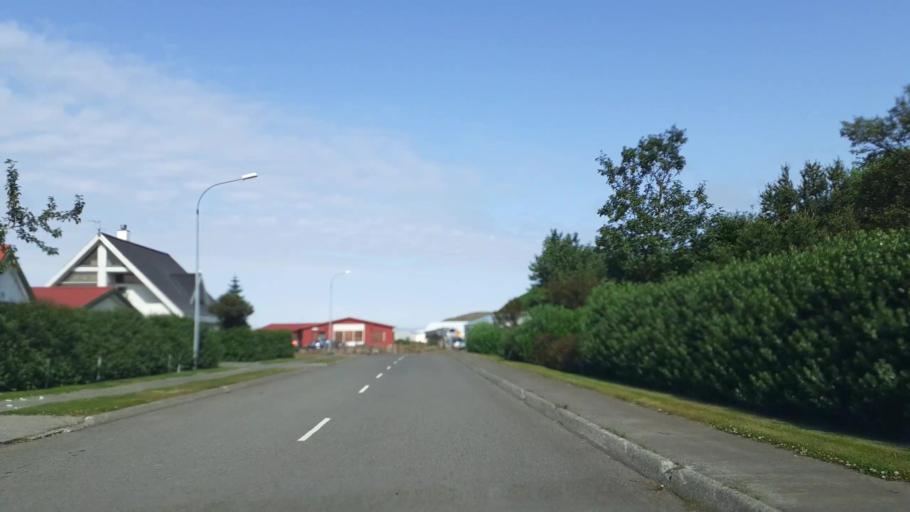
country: IS
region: Northwest
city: Saudarkrokur
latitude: 65.6642
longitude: -20.2903
